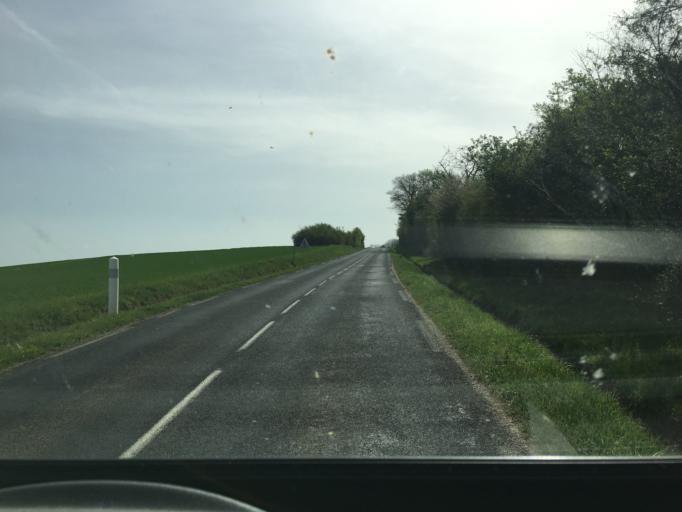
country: FR
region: Lorraine
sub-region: Departement de Meurthe-et-Moselle
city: Gondreville
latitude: 48.6629
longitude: 5.9625
